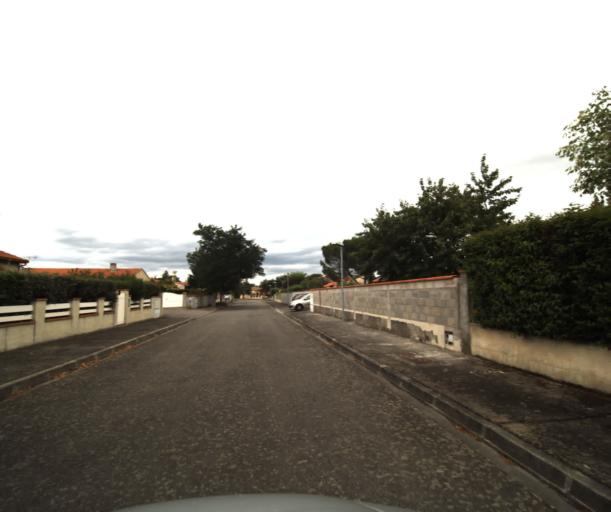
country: FR
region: Midi-Pyrenees
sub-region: Departement de la Haute-Garonne
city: Roquettes
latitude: 43.4735
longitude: 1.3762
